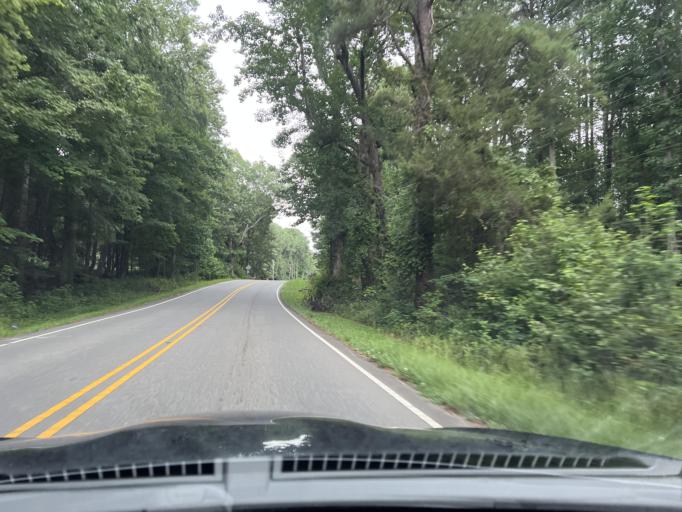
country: US
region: North Carolina
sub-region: Wake County
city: Wake Forest
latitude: 36.0117
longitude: -78.5425
